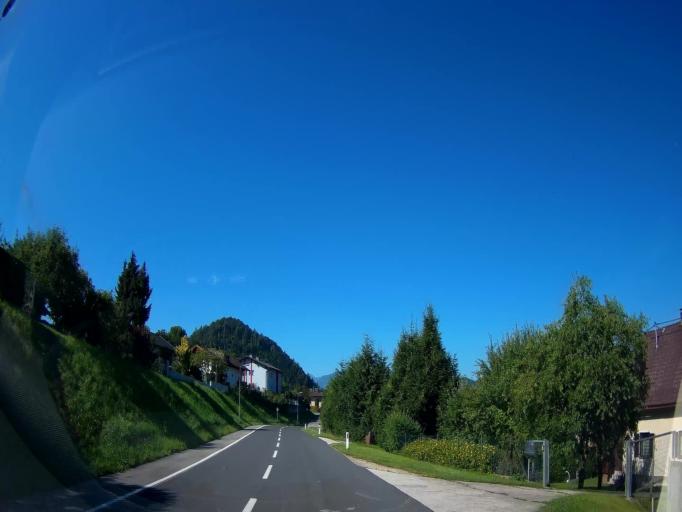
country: AT
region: Carinthia
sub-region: Politischer Bezirk Volkermarkt
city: Gallizien
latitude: 46.6098
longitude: 14.5393
